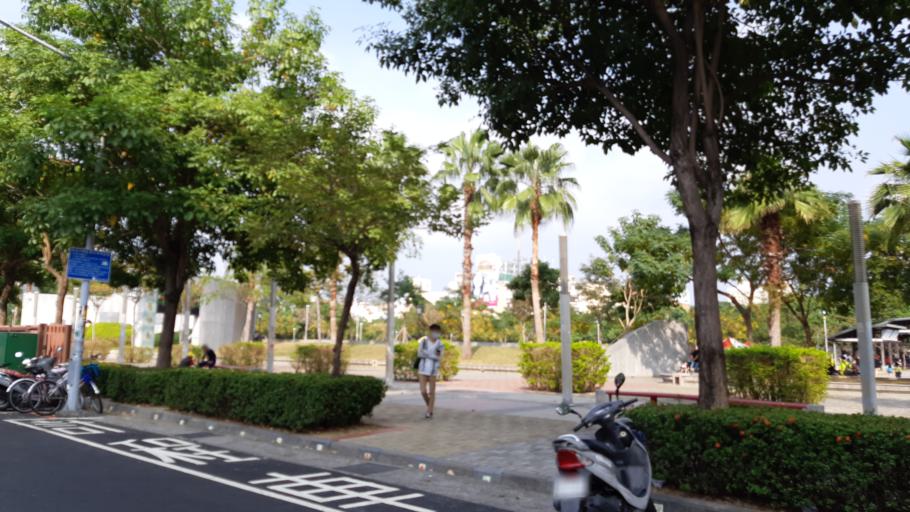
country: TW
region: Taiwan
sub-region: Chiayi
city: Jiayi Shi
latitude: 23.4743
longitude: 120.4503
